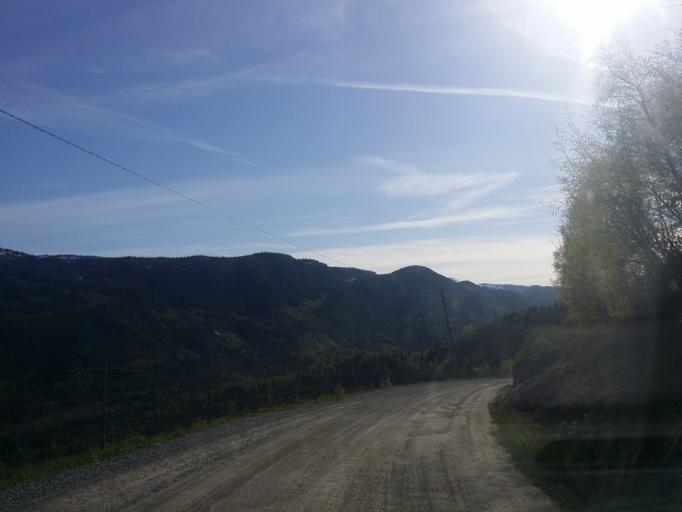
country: NO
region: Telemark
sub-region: Seljord
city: Seljord
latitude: 59.6102
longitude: 8.6877
